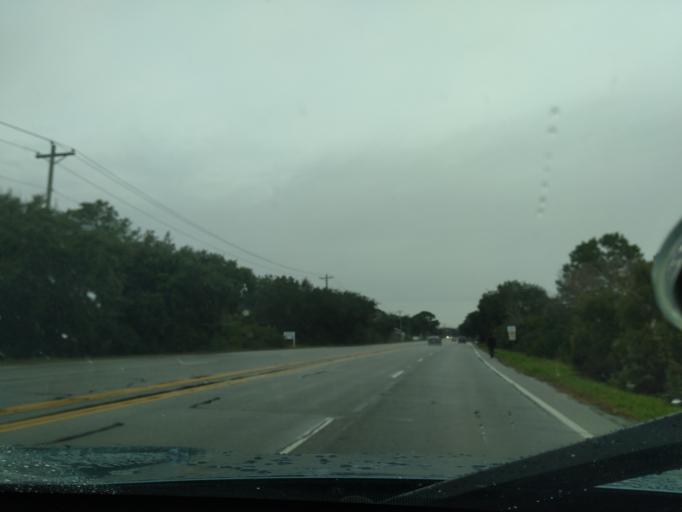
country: US
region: South Carolina
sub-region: Charleston County
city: Folly Beach
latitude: 32.6900
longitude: -79.9627
